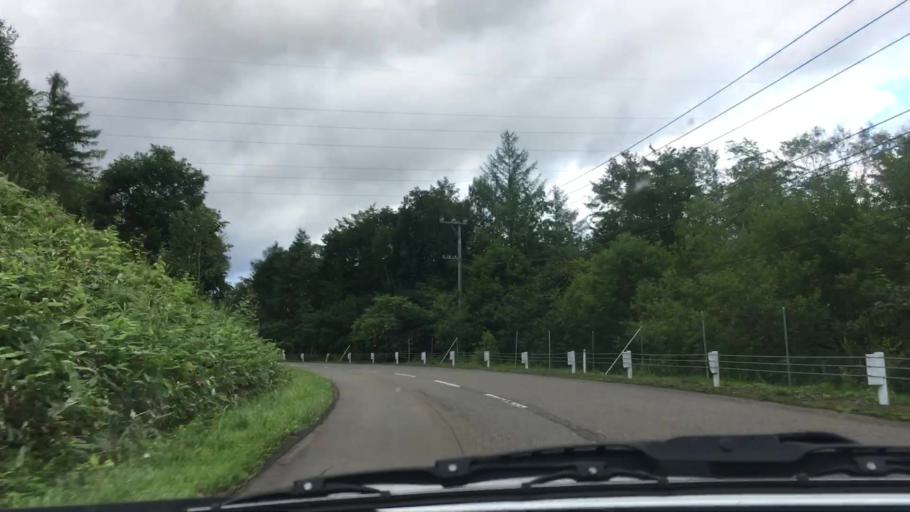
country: JP
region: Hokkaido
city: Otofuke
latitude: 43.1567
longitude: 142.8545
